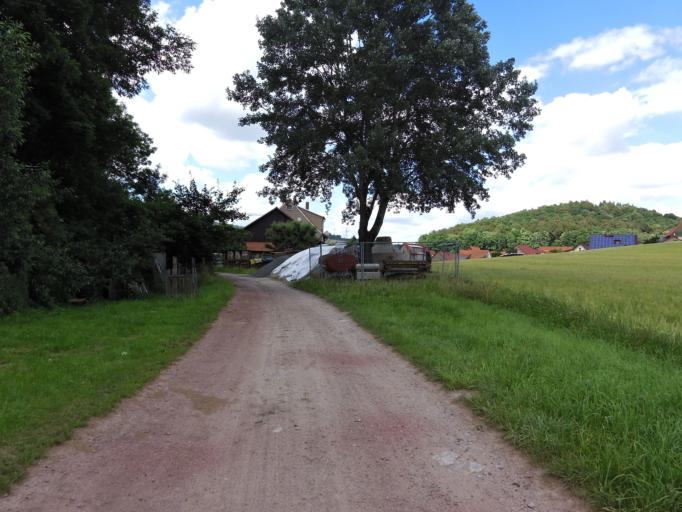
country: DE
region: Hesse
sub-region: Regierungsbezirk Kassel
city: Herleshausen
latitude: 50.9957
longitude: 10.2155
